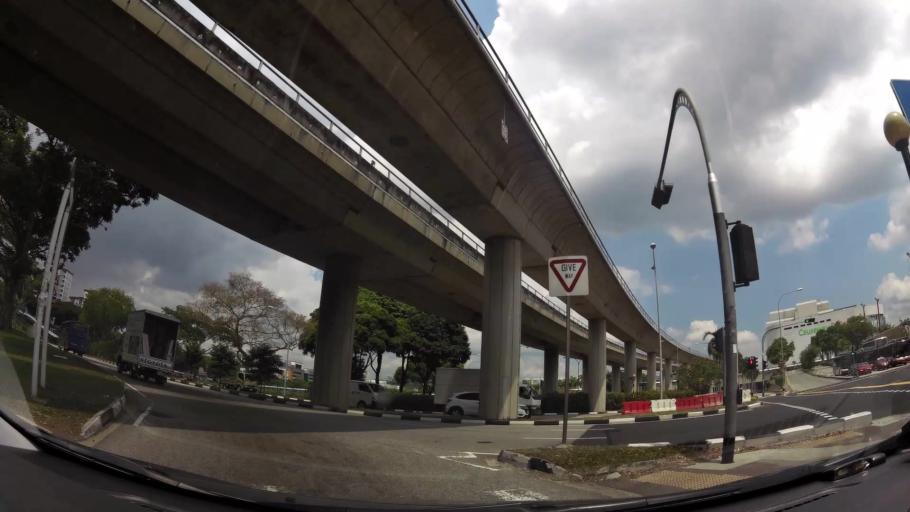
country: MY
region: Johor
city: Johor Bahru
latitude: 1.4354
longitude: 103.7831
